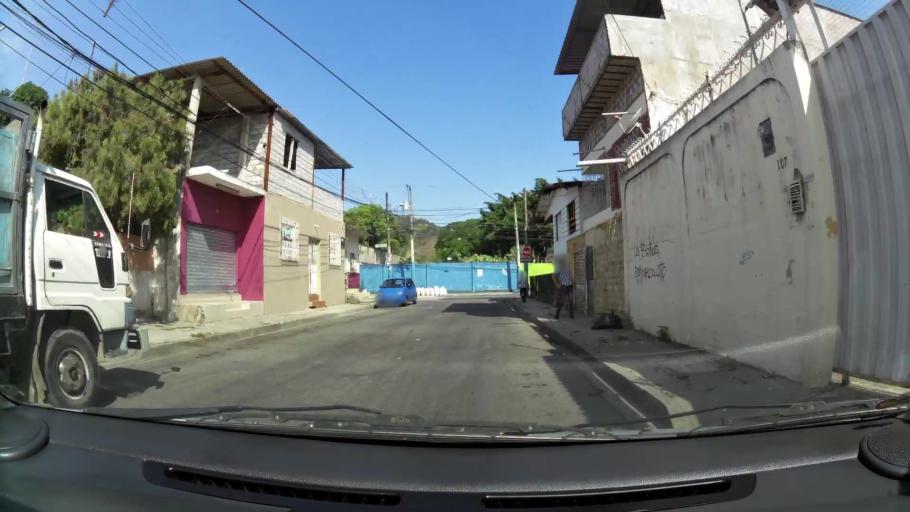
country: EC
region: Guayas
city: Guayaquil
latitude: -2.1619
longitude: -79.9356
